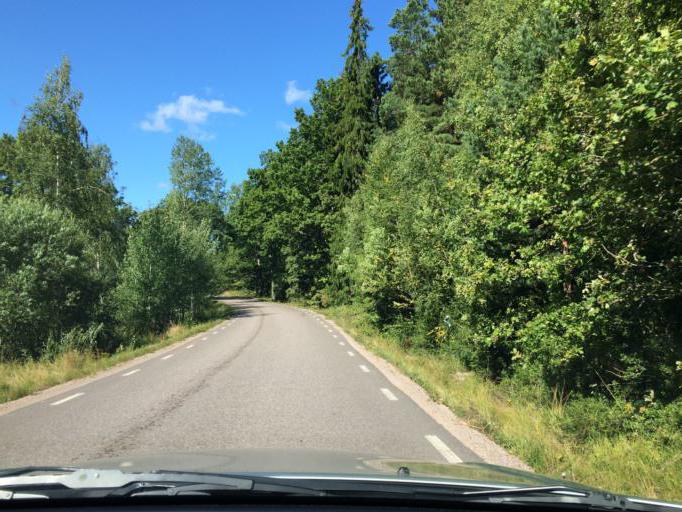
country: SE
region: Soedermanland
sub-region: Eskilstuna Kommun
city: Kvicksund
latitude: 59.4954
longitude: 16.3114
